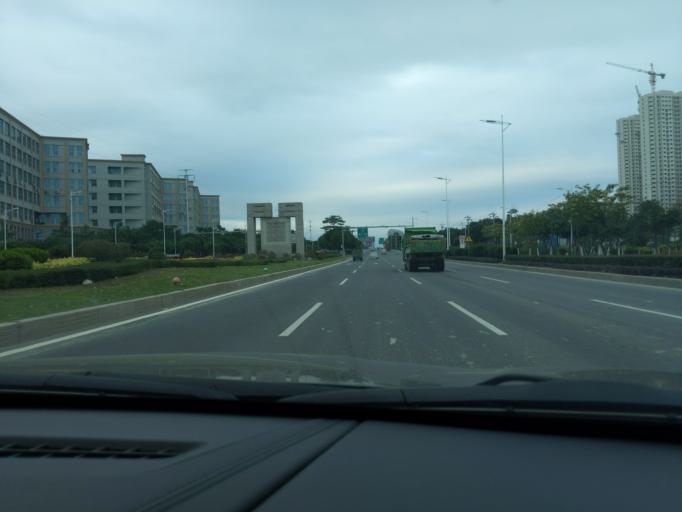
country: CN
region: Fujian
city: Maxiang
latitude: 24.6730
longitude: 118.2285
